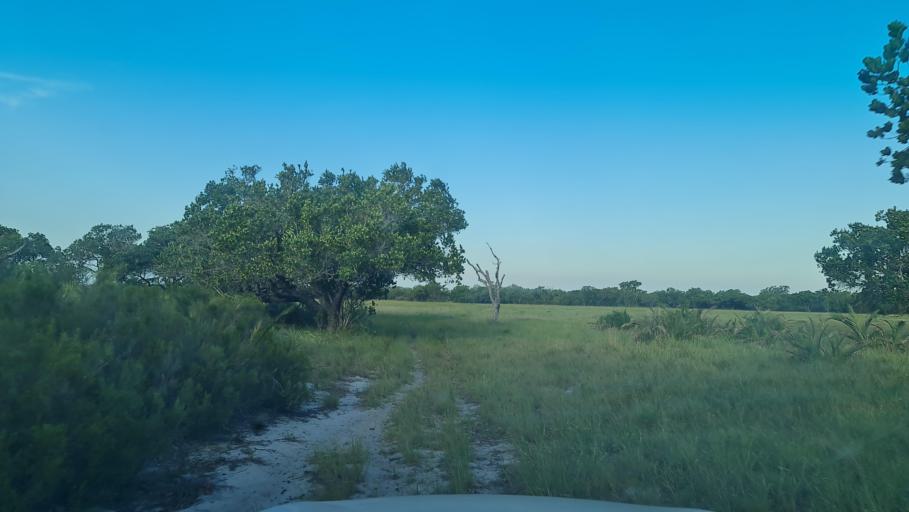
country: MZ
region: Gaza
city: Macia
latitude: -25.2230
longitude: 33.0283
